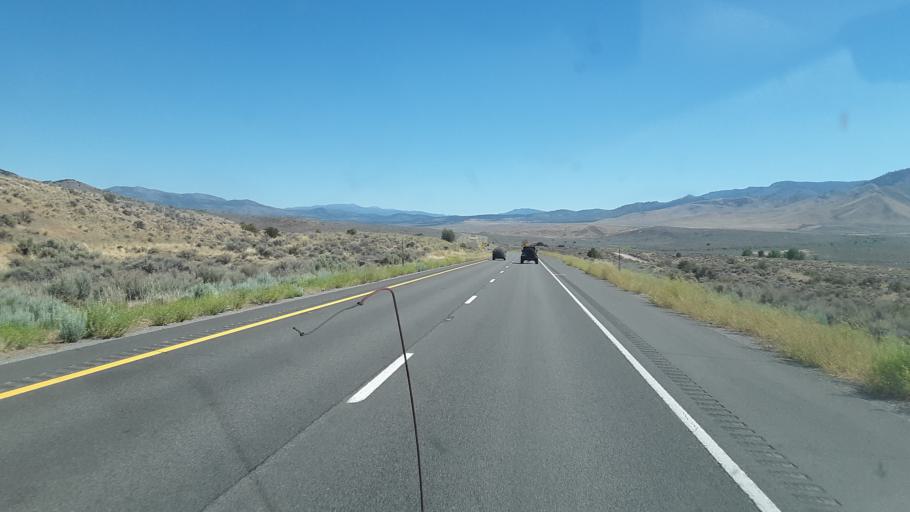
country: US
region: Nevada
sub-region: Washoe County
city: Cold Springs
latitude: 39.7452
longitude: -120.0398
